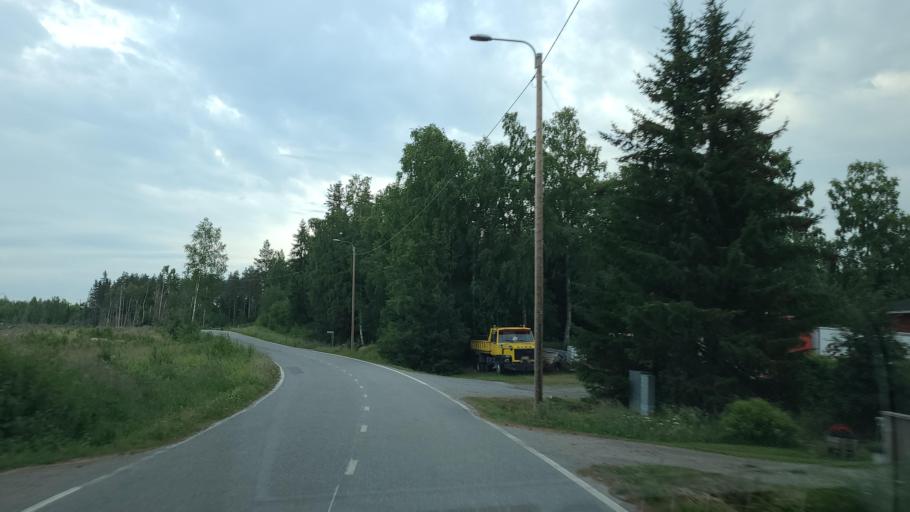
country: FI
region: Ostrobothnia
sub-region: Vaasa
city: Replot
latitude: 63.1684
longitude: 21.2615
